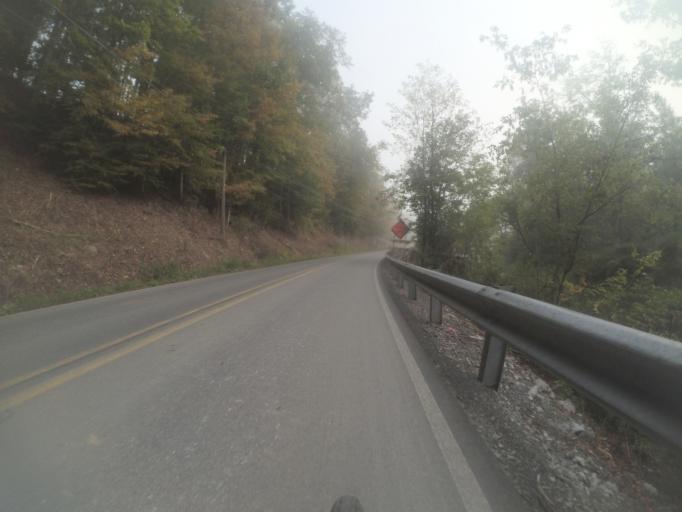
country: US
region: Pennsylvania
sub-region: Mifflin County
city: Milroy
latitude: 40.8659
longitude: -77.4596
